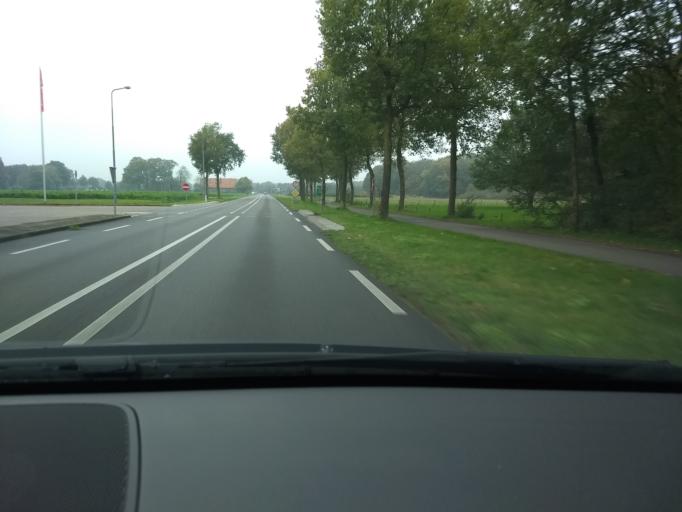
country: DE
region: North Rhine-Westphalia
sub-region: Regierungsbezirk Munster
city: Sudlohn
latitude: 51.9388
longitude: 6.7911
